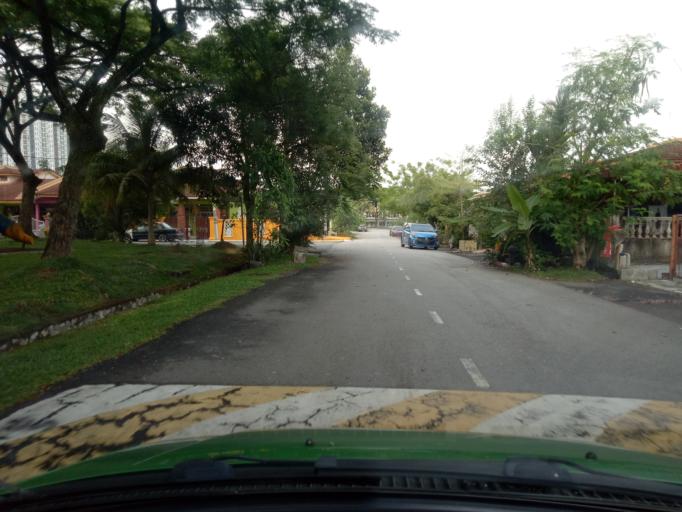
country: MY
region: Selangor
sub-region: Hulu Langat
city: Semenyih
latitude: 2.9280
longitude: 101.8616
